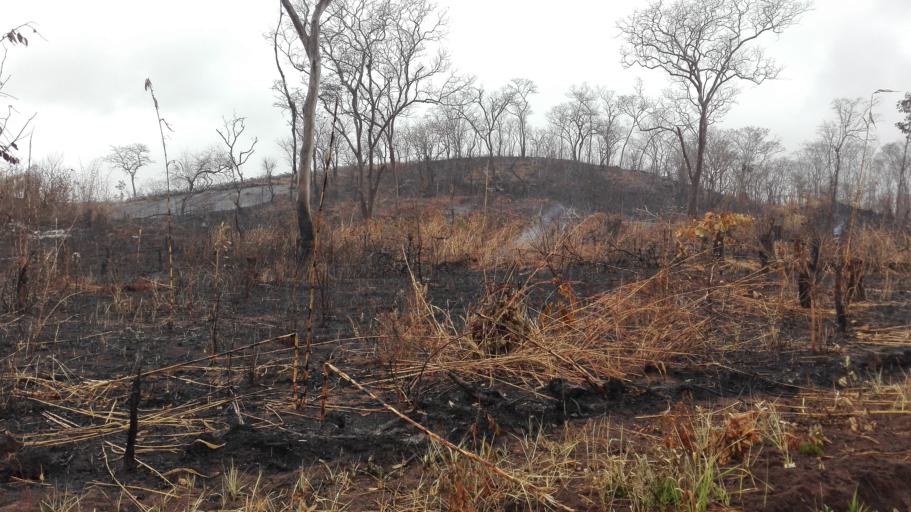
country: MZ
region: Nampula
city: Mutuali
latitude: -15.6476
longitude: 36.8142
